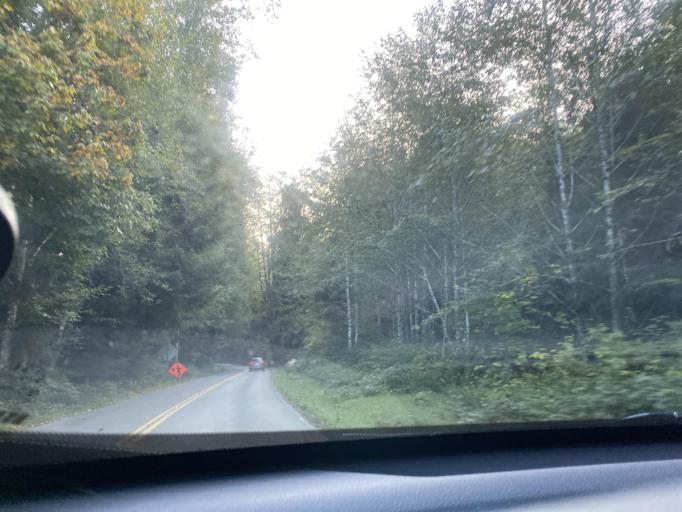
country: US
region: Washington
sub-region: Clallam County
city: Forks
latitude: 47.8147
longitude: -124.0663
